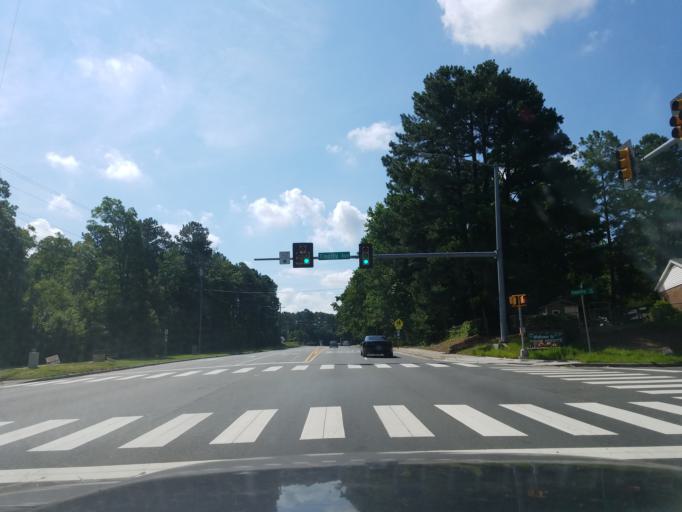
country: US
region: North Carolina
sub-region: Durham County
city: Durham
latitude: 35.9573
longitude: -78.9092
